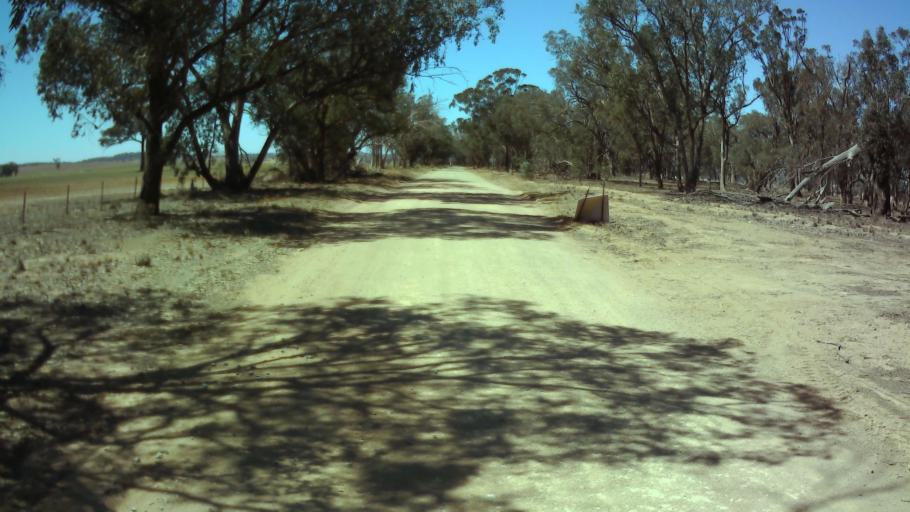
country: AU
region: New South Wales
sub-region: Weddin
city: Grenfell
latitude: -33.8739
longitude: 148.0887
